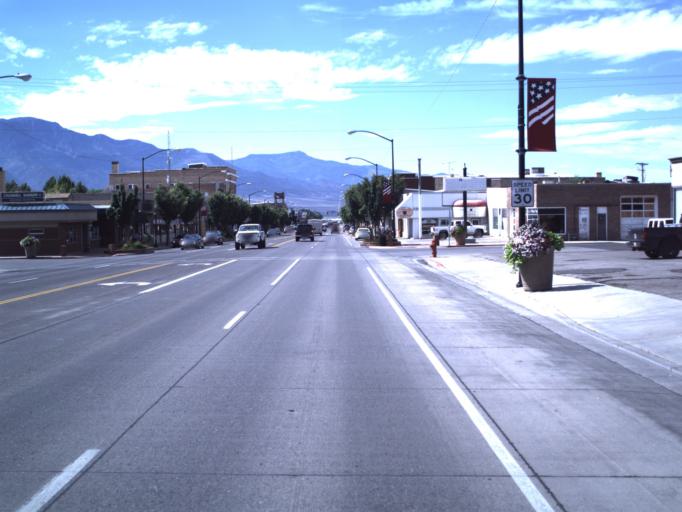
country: US
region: Utah
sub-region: Sevier County
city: Richfield
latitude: 38.7714
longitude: -112.0849
